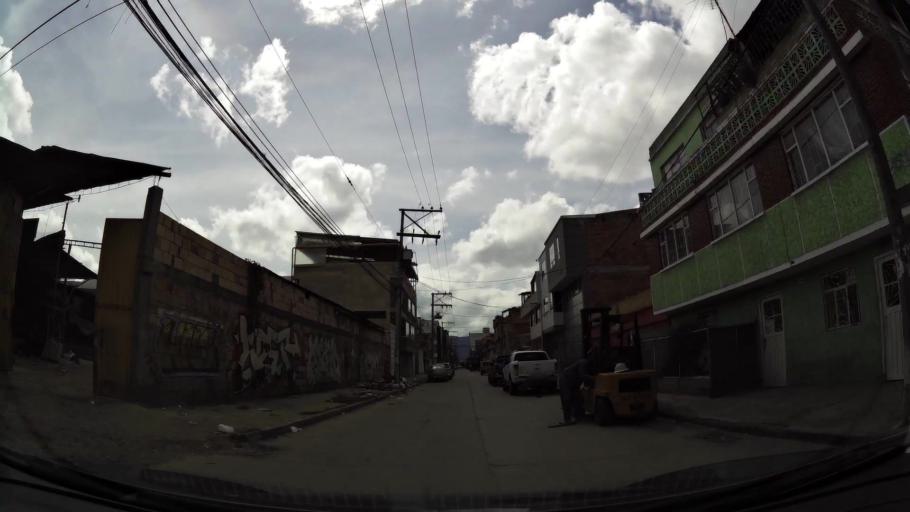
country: CO
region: Bogota D.C.
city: Bogota
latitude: 4.6933
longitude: -74.1133
